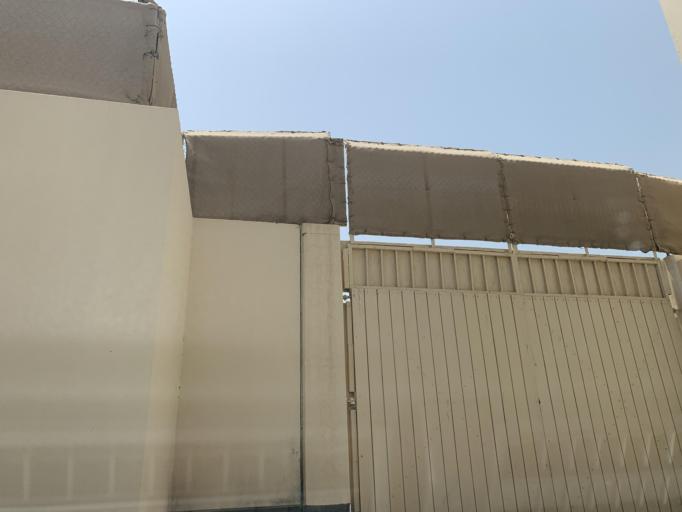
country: BH
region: Northern
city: Sitrah
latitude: 26.1475
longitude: 50.5862
